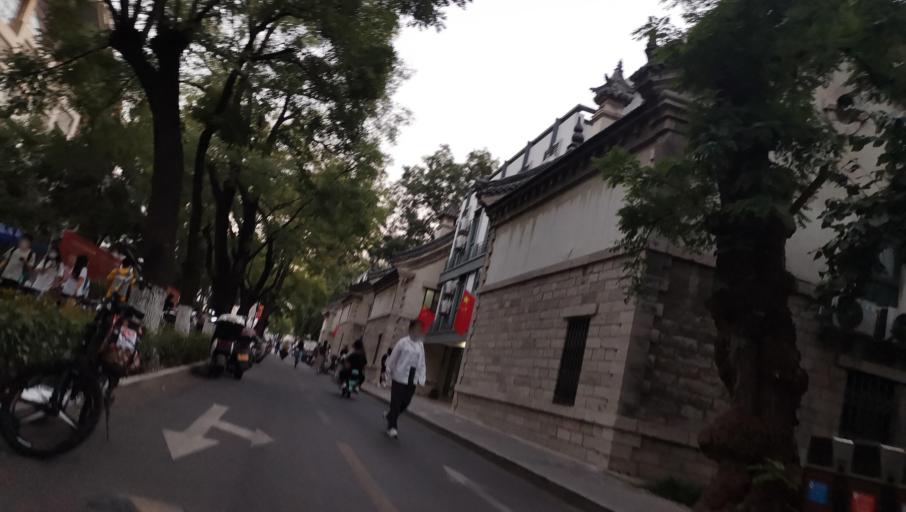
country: CN
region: Shandong Sheng
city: Jinan
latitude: 36.6540
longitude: 117.0130
